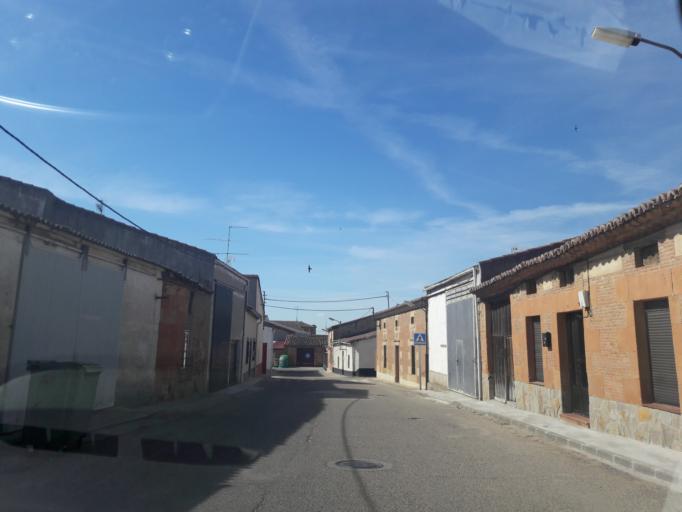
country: ES
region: Castille and Leon
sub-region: Provincia de Salamanca
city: Villoruela
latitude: 41.0095
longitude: -5.3949
